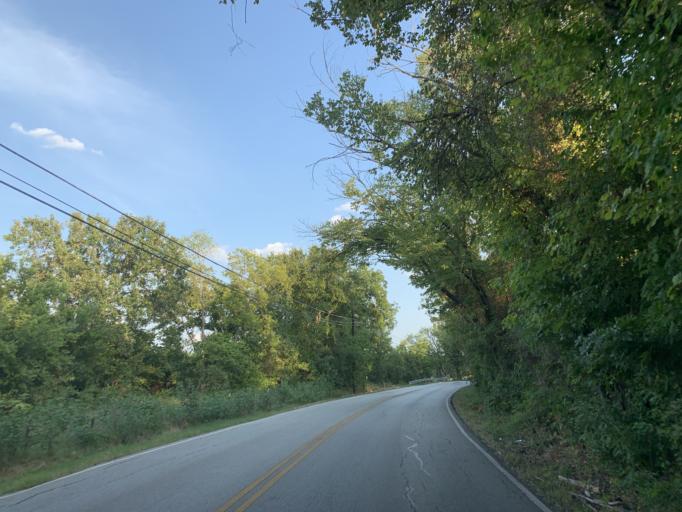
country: US
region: Texas
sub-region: Tarrant County
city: Hurst
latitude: 32.7786
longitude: -97.1754
